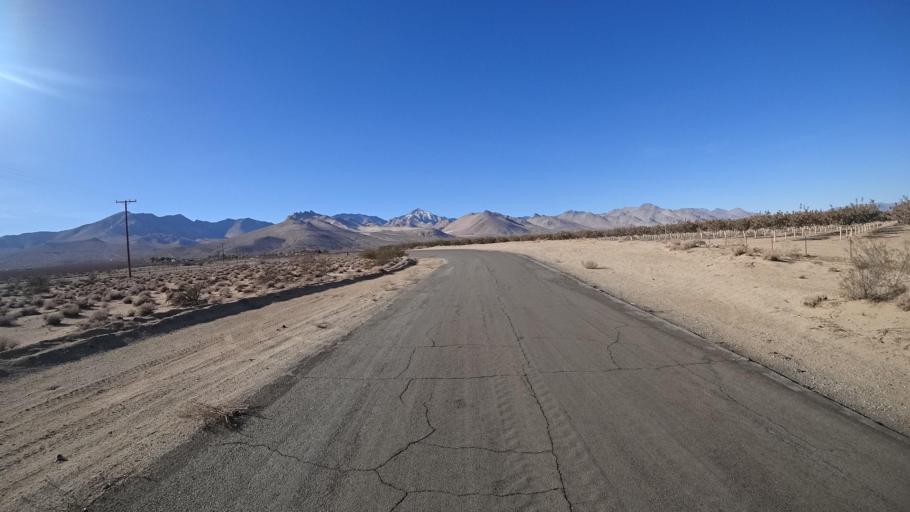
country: US
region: California
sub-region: Kern County
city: Inyokern
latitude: 35.6814
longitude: -117.8407
